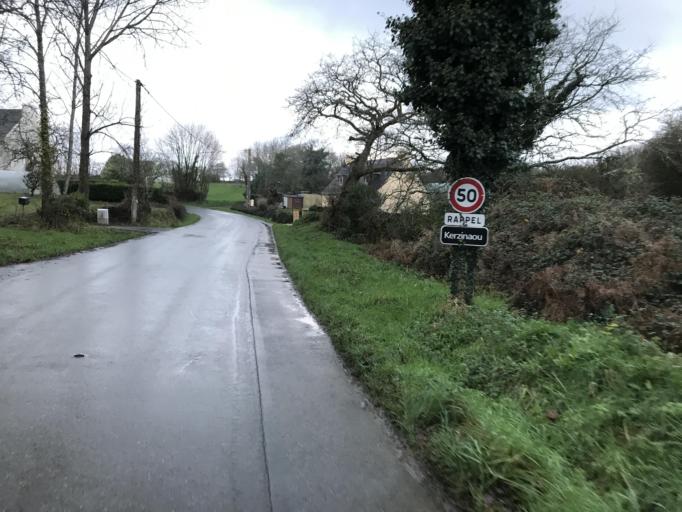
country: FR
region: Brittany
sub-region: Departement du Finistere
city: Plougastel-Daoulas
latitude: 48.3590
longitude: -4.3432
